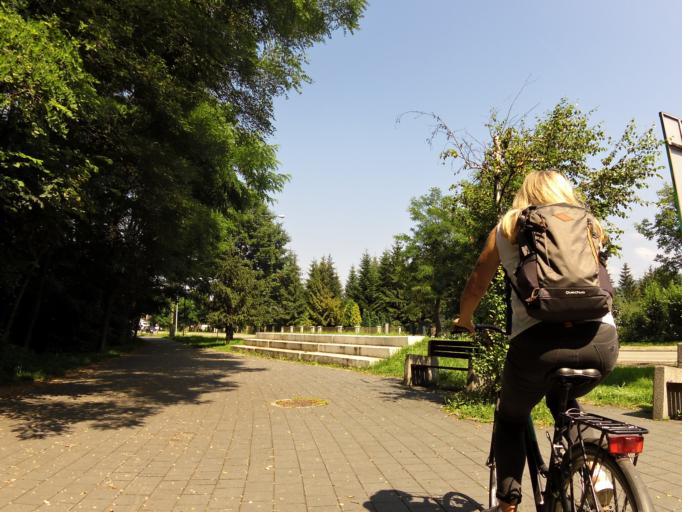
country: PL
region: Silesian Voivodeship
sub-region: Powiat zywiecki
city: Wegierska Gorka
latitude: 49.6104
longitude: 19.1249
